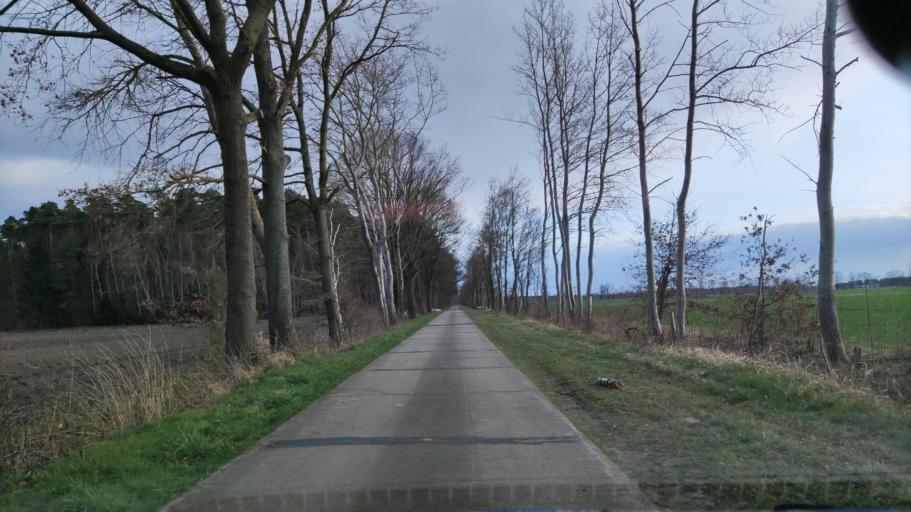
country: DE
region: Lower Saxony
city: Trebel
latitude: 53.0195
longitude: 11.2697
